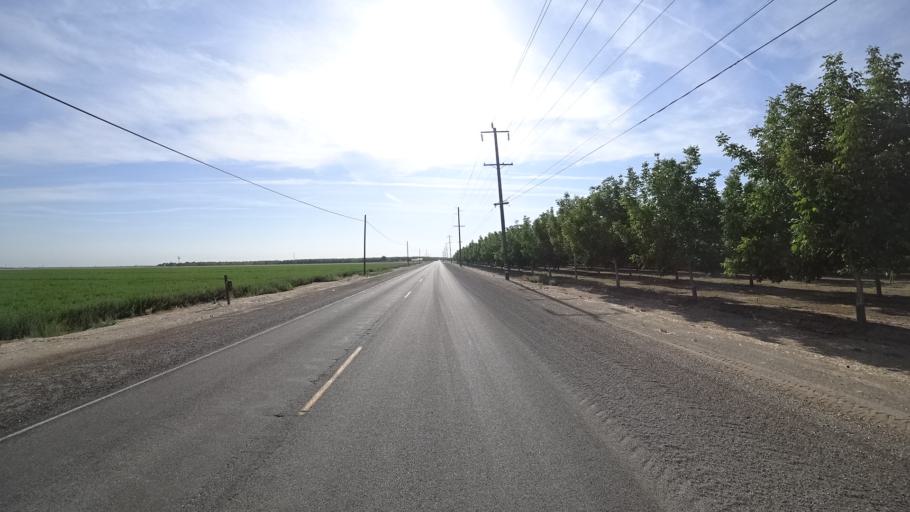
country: US
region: California
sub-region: Tulare County
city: Goshen
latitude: 36.3427
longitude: -119.5006
